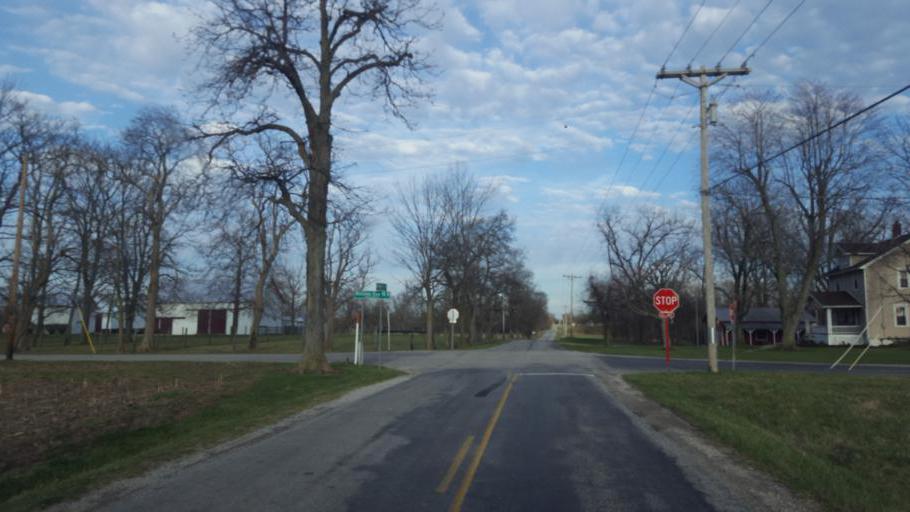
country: US
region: Ohio
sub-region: Morrow County
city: Cardington
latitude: 40.6018
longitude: -82.9788
